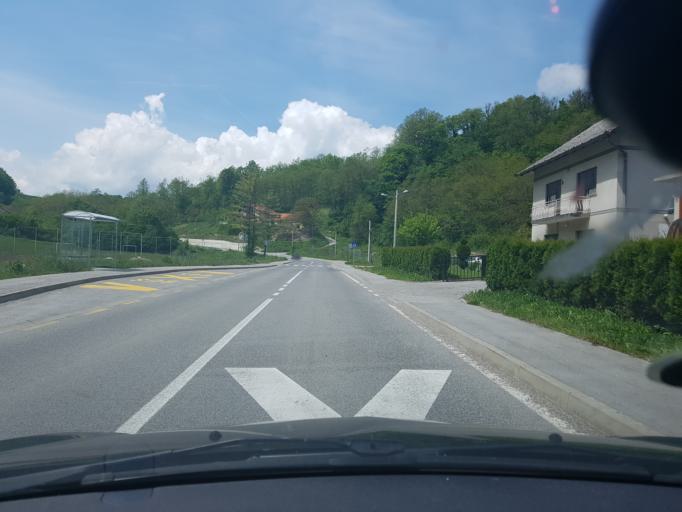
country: HR
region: Krapinsko-Zagorska
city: Pregrada
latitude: 46.1890
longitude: 15.7398
